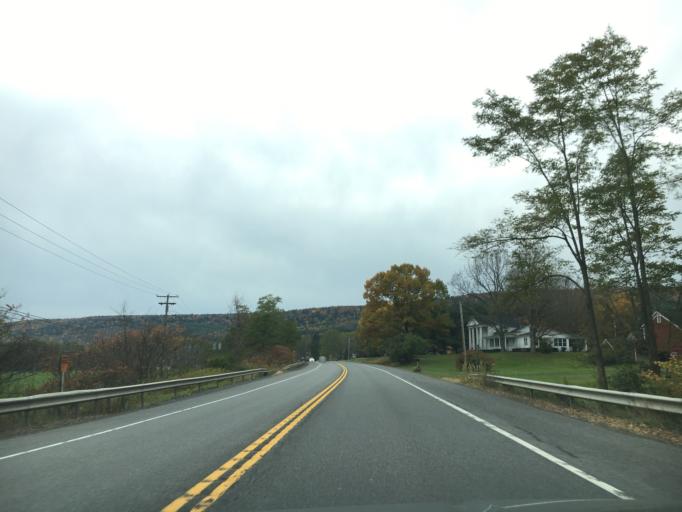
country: US
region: New York
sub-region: Otsego County
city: Oneonta
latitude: 42.5235
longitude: -74.9894
